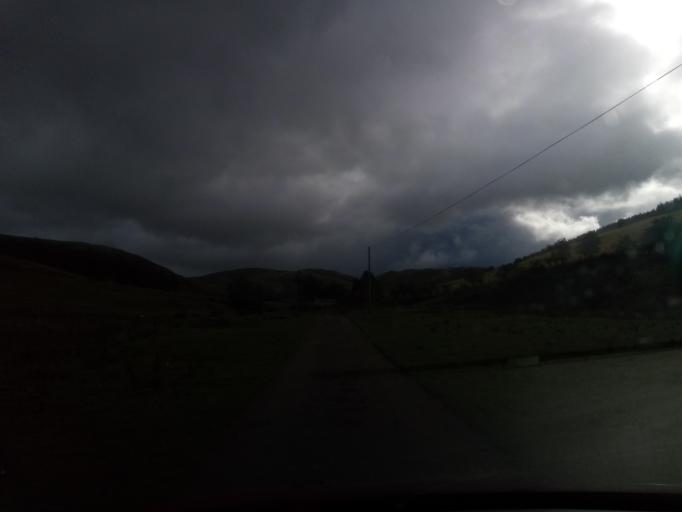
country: GB
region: Scotland
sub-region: The Scottish Borders
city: Coldstream
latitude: 55.5395
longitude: -2.2540
